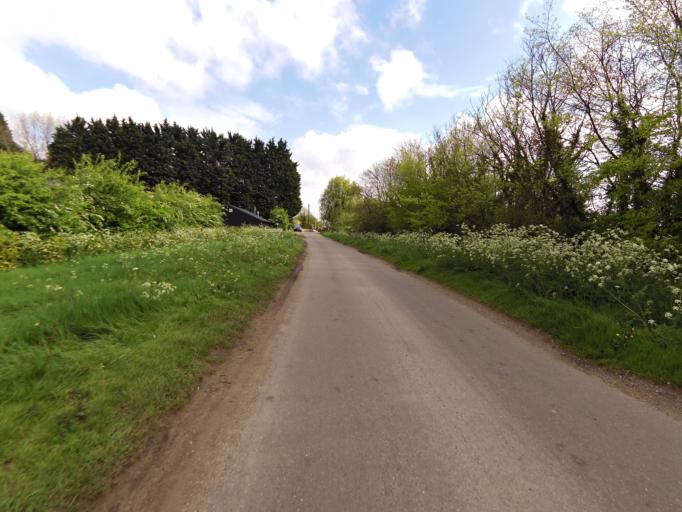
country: GB
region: England
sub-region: Cambridgeshire
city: Bottisham
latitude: 52.2450
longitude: 0.2415
